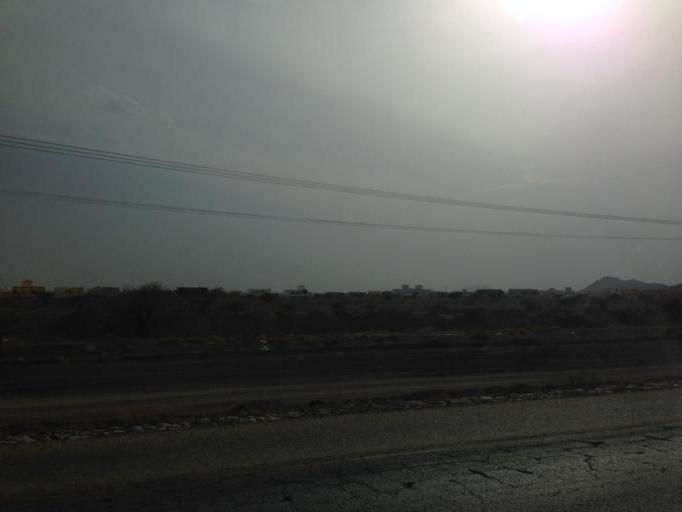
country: OM
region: Ash Sharqiyah
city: Al Qabil
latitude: 22.6282
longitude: 58.6508
